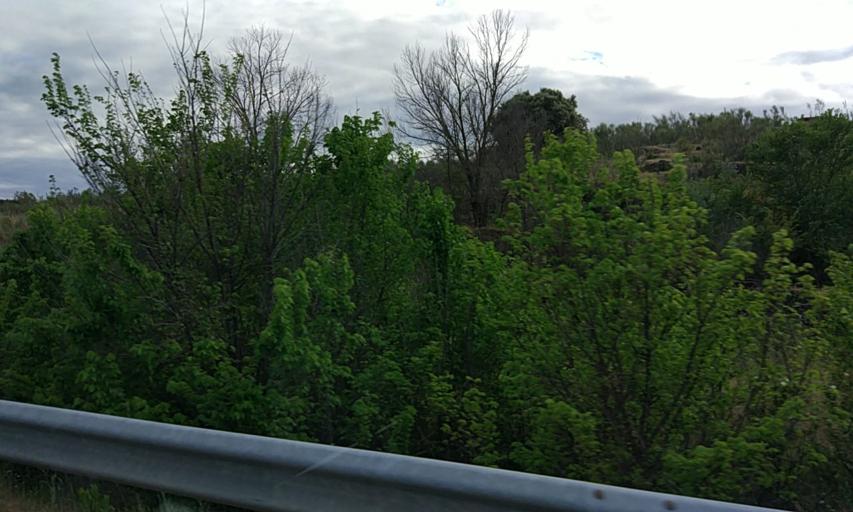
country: ES
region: Extremadura
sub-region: Provincia de Caceres
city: Coria
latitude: 39.9546
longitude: -6.5104
